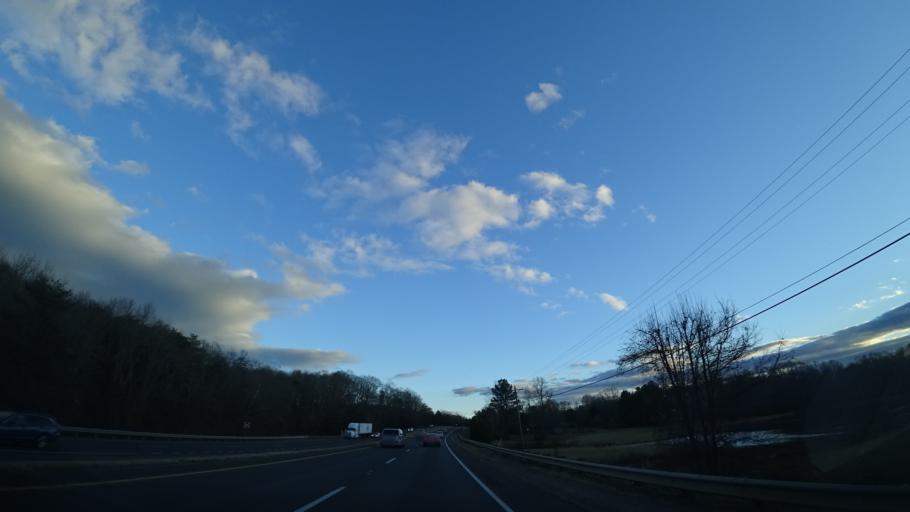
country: US
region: Virginia
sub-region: Fauquier County
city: Bealeton
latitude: 38.4975
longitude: -77.6893
